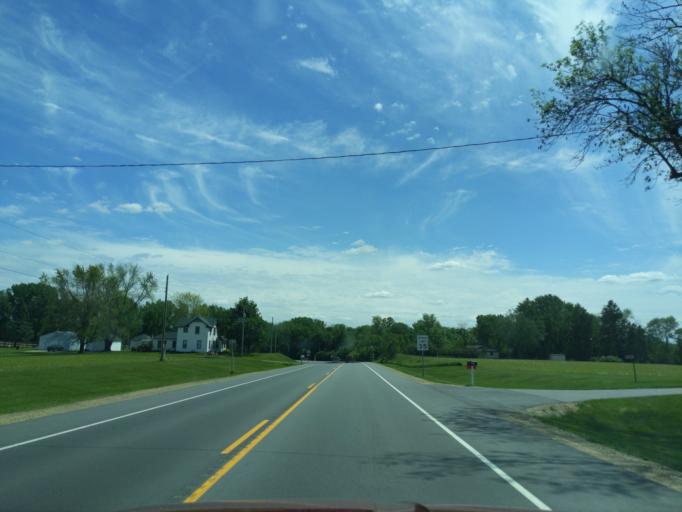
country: US
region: Wisconsin
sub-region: Columbia County
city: Pardeeville
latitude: 43.5488
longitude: -89.3059
